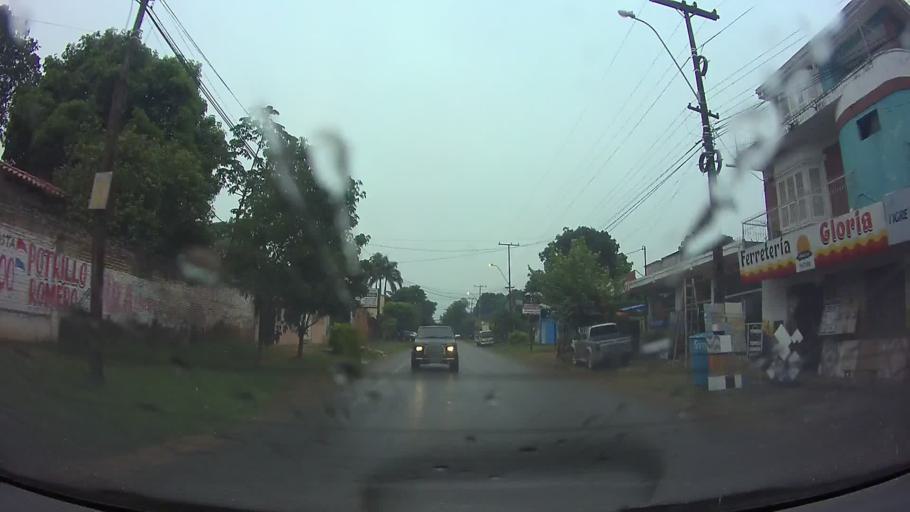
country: PY
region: Central
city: Ita
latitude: -25.5061
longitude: -57.3577
